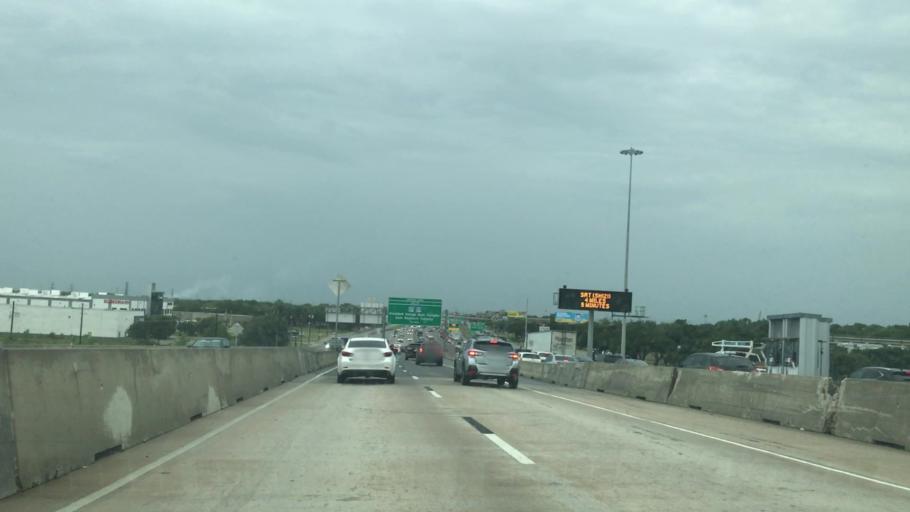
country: US
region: Texas
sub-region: Dallas County
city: Carrollton
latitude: 32.9562
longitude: -96.9126
